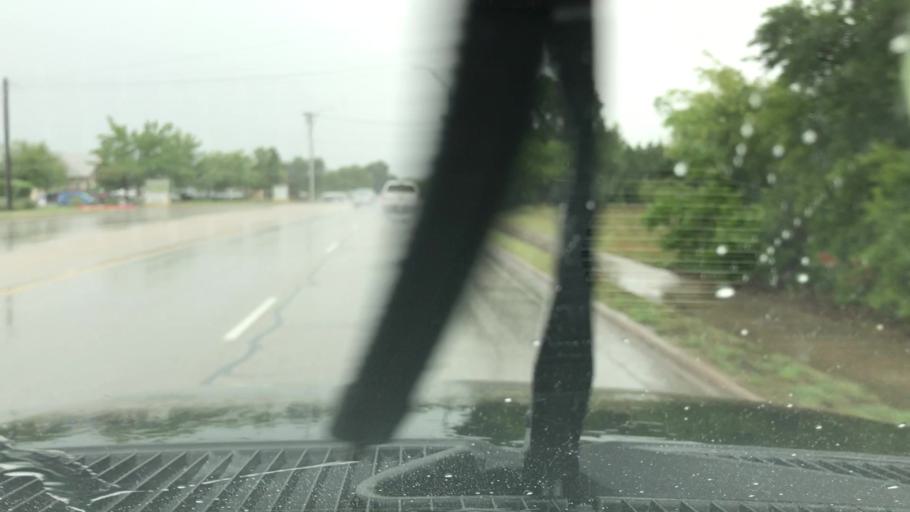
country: US
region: Texas
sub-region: Williamson County
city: Cedar Park
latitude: 30.4922
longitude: -97.8280
